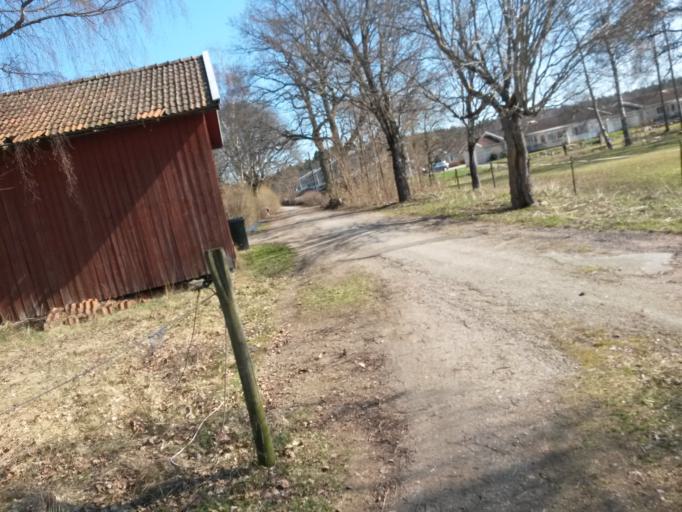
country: SE
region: Vaestra Goetaland
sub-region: Vargarda Kommun
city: Vargarda
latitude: 58.0423
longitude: 12.8100
